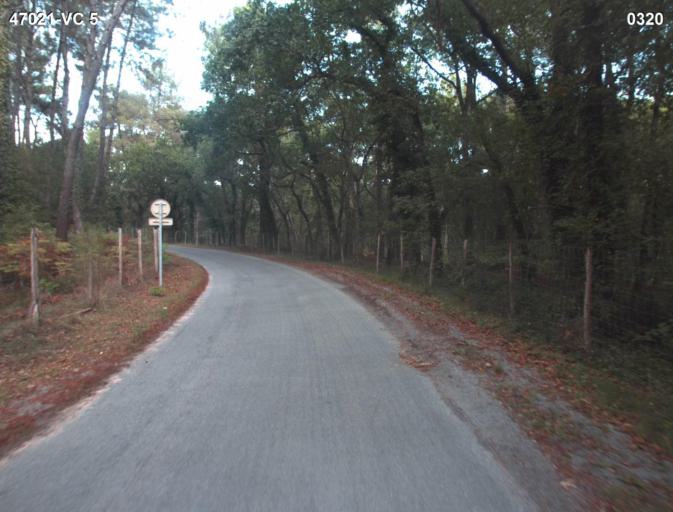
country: FR
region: Aquitaine
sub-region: Departement du Lot-et-Garonne
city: Barbaste
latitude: 44.1394
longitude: 0.2901
